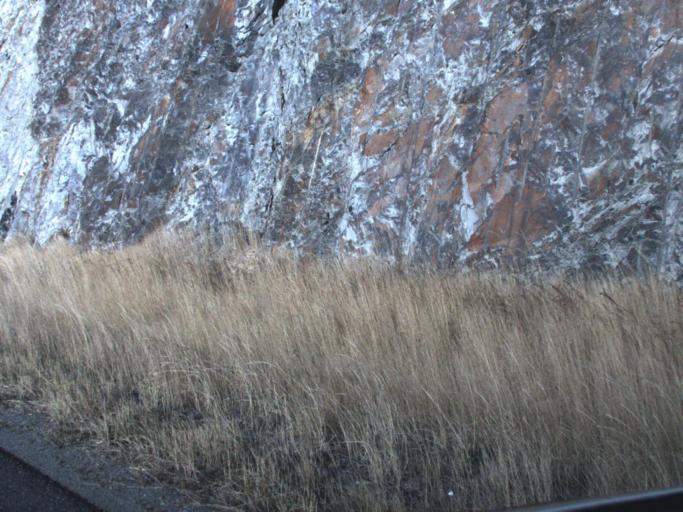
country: US
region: Washington
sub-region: Stevens County
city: Kettle Falls
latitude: 48.6331
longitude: -118.0807
